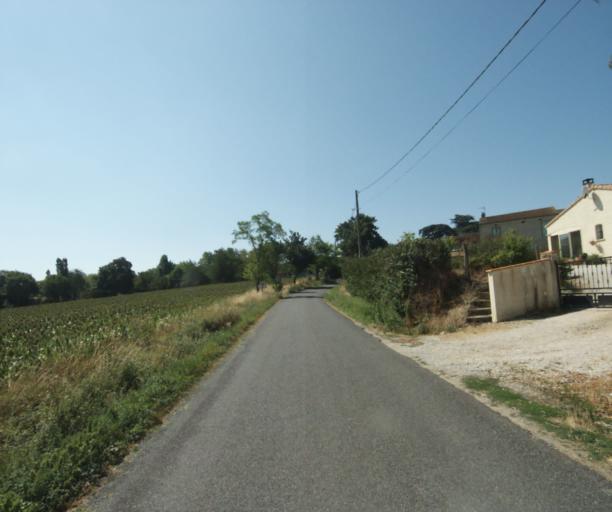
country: FR
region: Midi-Pyrenees
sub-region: Departement de la Haute-Garonne
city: Revel
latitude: 43.5054
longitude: 1.9492
